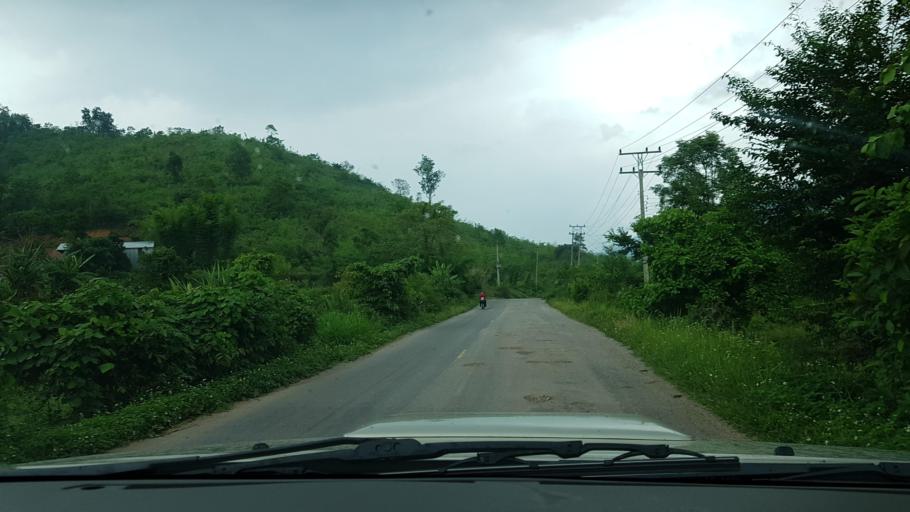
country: LA
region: Oudomxai
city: Muang Xay
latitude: 20.6214
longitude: 101.9577
